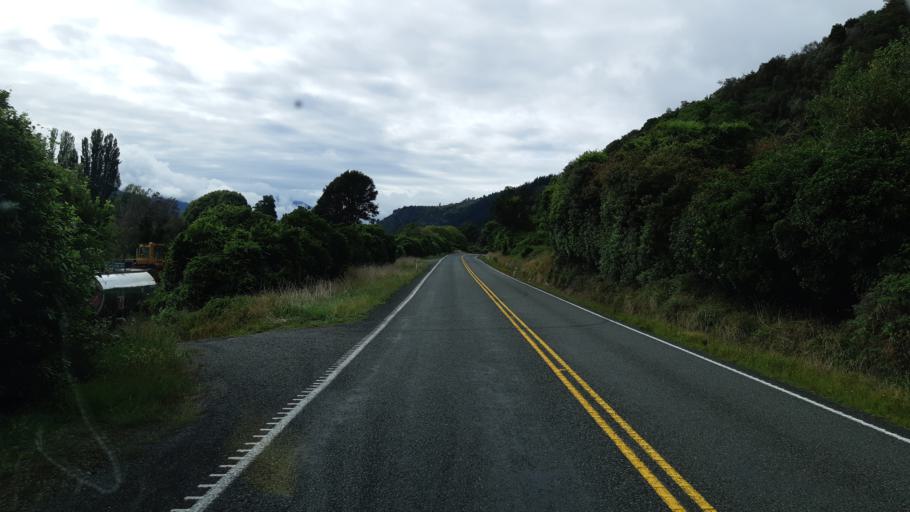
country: NZ
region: West Coast
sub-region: Buller District
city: Westport
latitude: -41.7760
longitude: 172.2415
